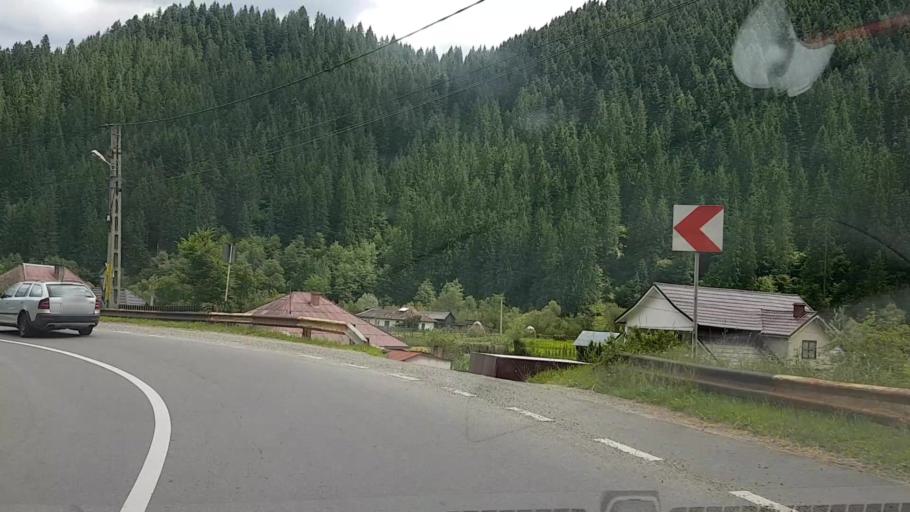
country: RO
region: Neamt
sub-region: Comuna Farcasa
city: Farcasa
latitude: 47.1491
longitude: 25.8481
